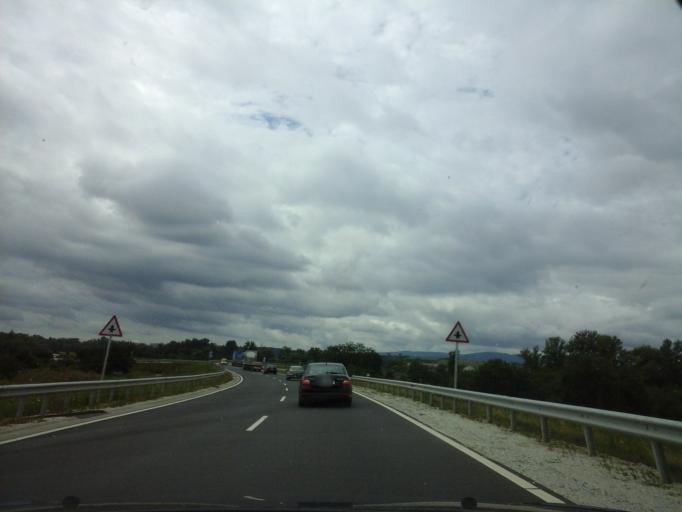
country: HU
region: Borsod-Abauj-Zemplen
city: Szirmabesenyo
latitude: 48.1335
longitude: 20.8106
